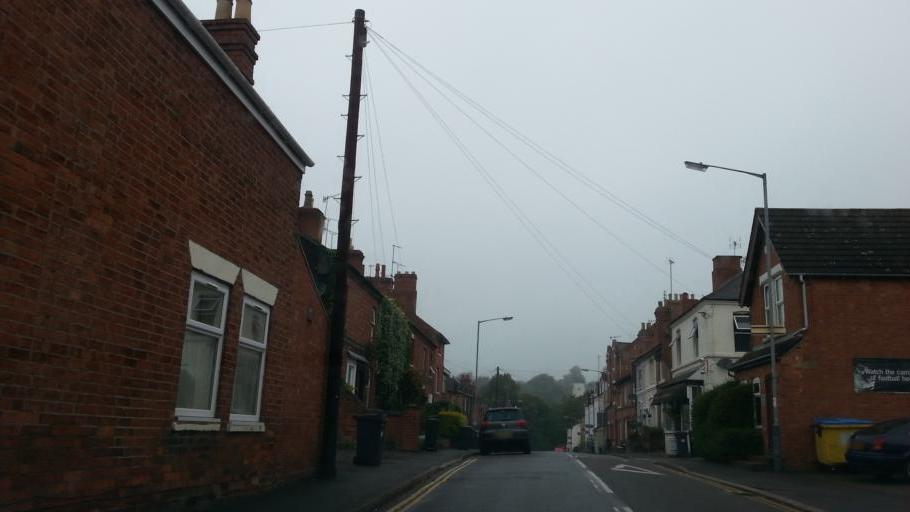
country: GB
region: England
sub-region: Warwickshire
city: Kenilworth
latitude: 52.3503
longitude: -1.5718
